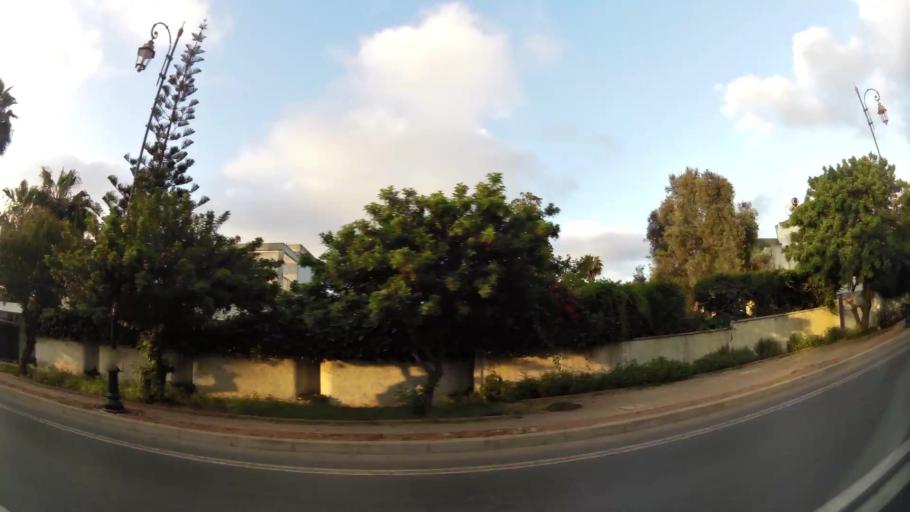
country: MA
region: Rabat-Sale-Zemmour-Zaer
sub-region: Rabat
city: Rabat
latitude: 33.9750
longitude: -6.8361
